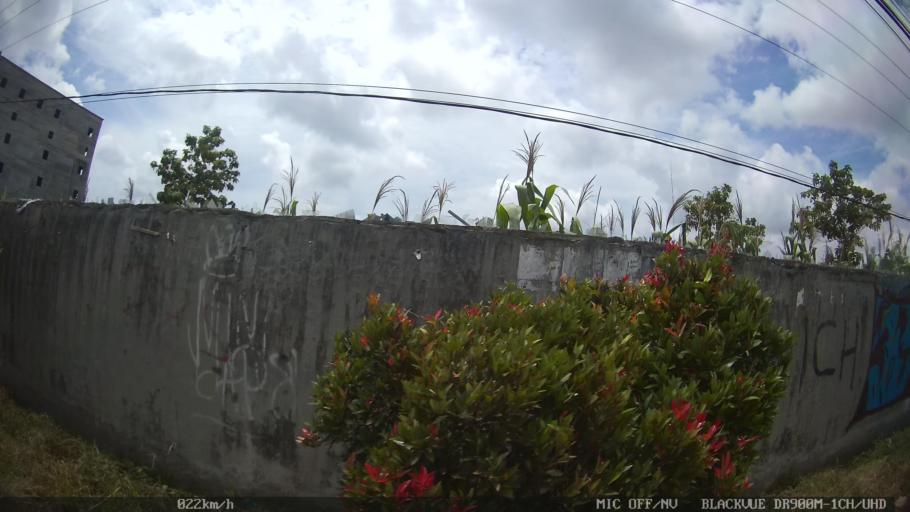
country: ID
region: North Sumatra
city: Medan
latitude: 3.6203
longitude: 98.7470
